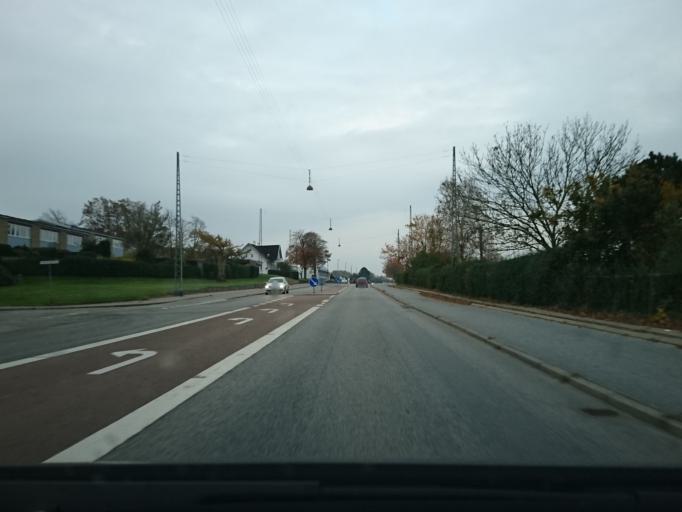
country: DK
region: North Denmark
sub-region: Alborg Kommune
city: Aalborg
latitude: 57.0236
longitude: 9.9269
